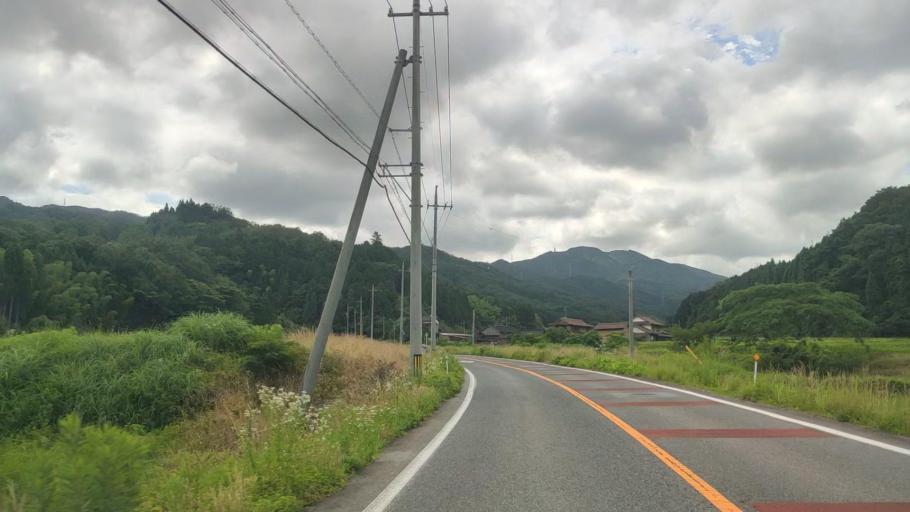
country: JP
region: Tottori
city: Yonago
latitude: 35.2953
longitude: 133.4160
